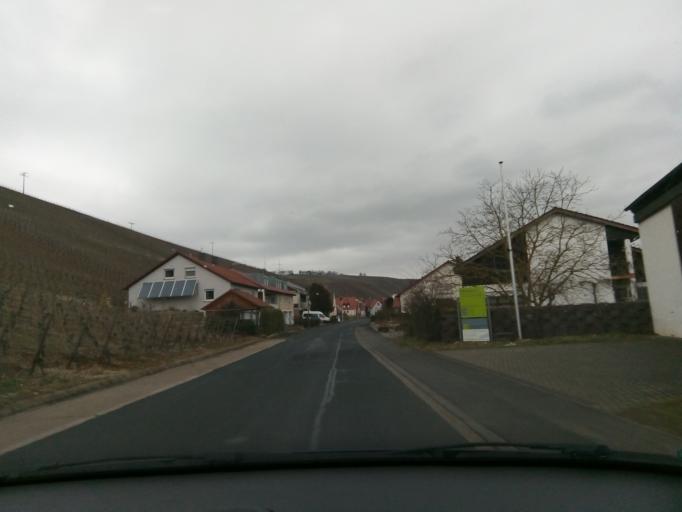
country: DE
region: Bavaria
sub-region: Regierungsbezirk Unterfranken
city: Nordheim
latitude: 49.8580
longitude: 10.1700
